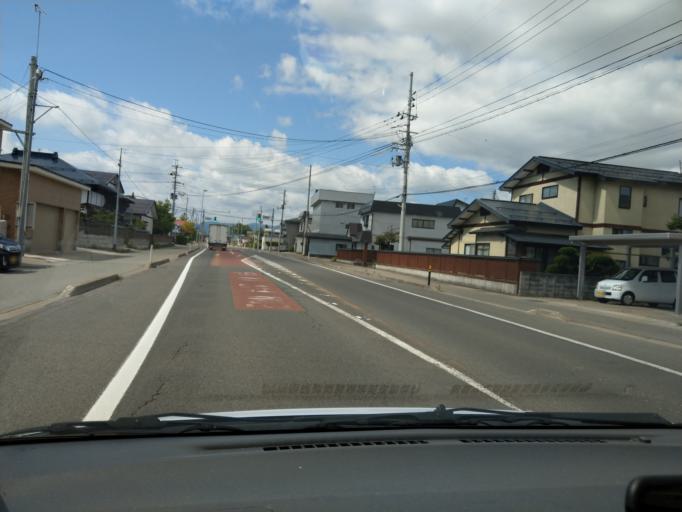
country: JP
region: Akita
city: Yuzawa
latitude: 39.1988
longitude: 140.5051
